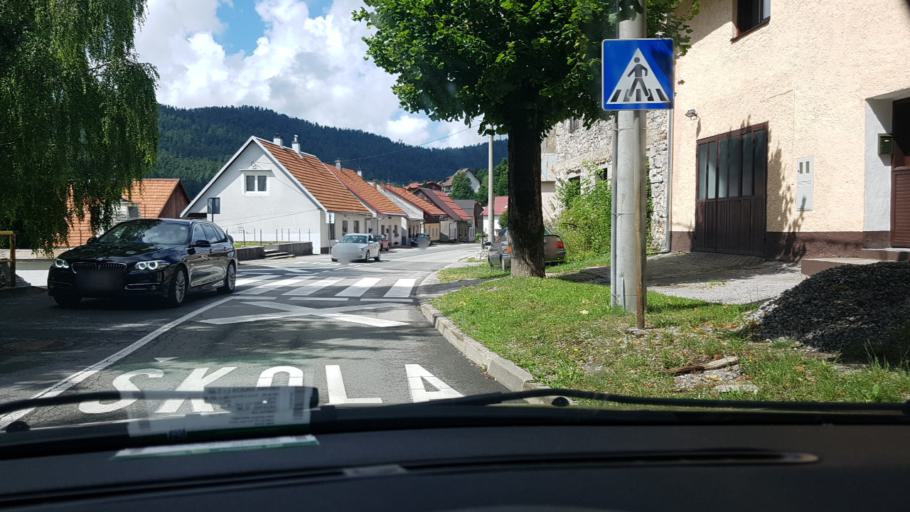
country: HR
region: Primorsko-Goranska
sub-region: Grad Delnice
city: Delnice
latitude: 45.3588
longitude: 14.7516
